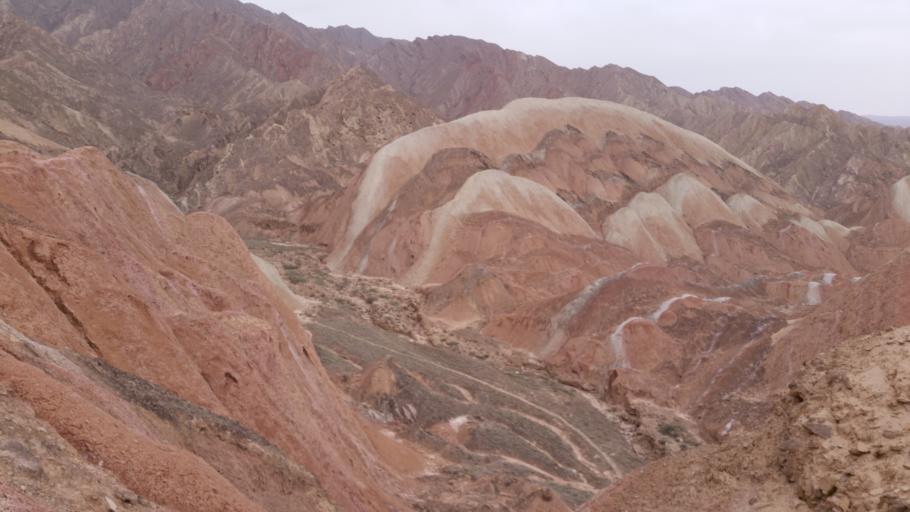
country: CN
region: Gansu Sheng
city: Ganjun
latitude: 38.9640
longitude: 100.0304
